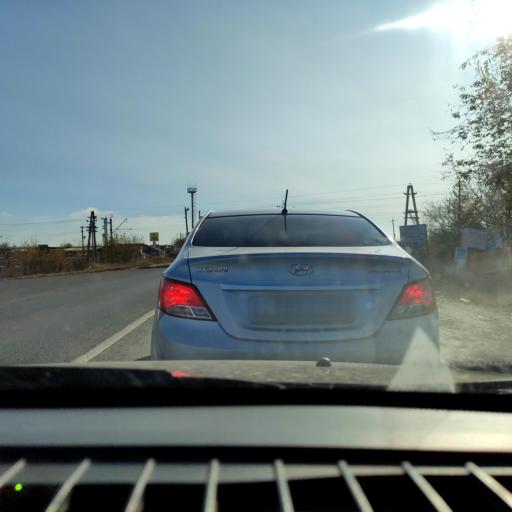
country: RU
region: Samara
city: Tol'yatti
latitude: 53.5624
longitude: 49.3553
